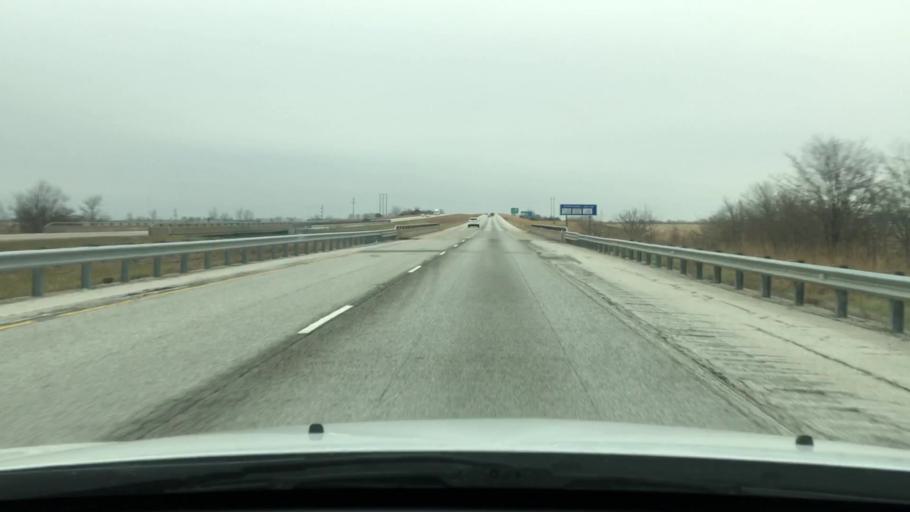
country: US
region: Illinois
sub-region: Morgan County
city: South Jacksonville
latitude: 39.7035
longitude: -90.1873
